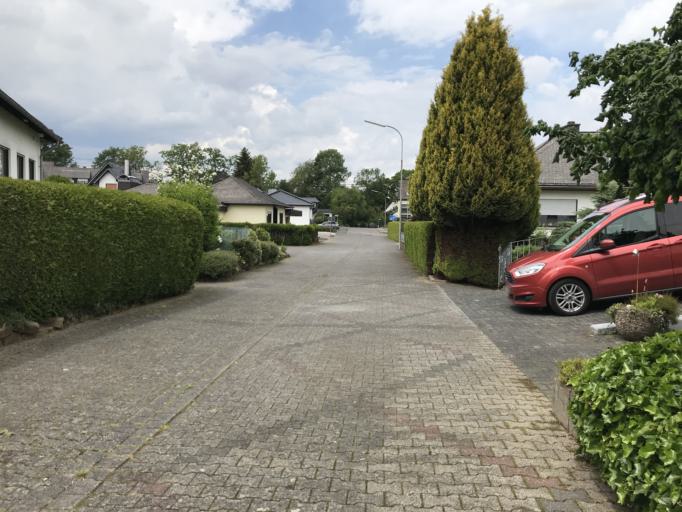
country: DE
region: Rheinland-Pfalz
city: Dierdorf
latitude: 50.5441
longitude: 7.6511
